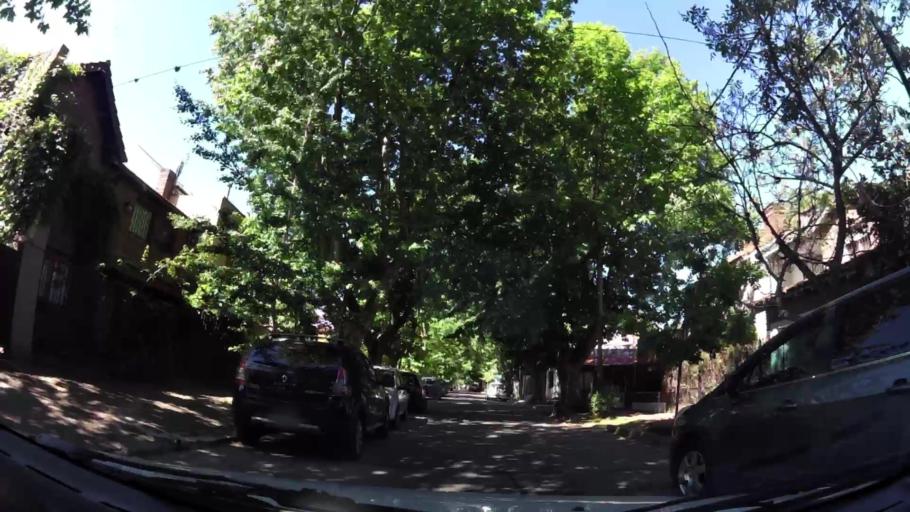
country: AR
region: Buenos Aires
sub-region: Partido de San Isidro
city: San Isidro
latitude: -34.4557
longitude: -58.5279
